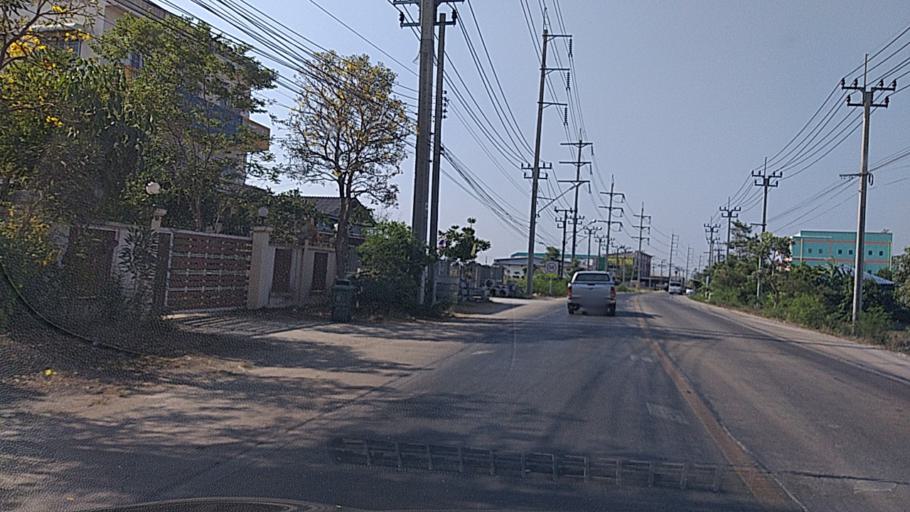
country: TH
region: Nonthaburi
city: Bang Yai
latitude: 13.8882
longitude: 100.3257
